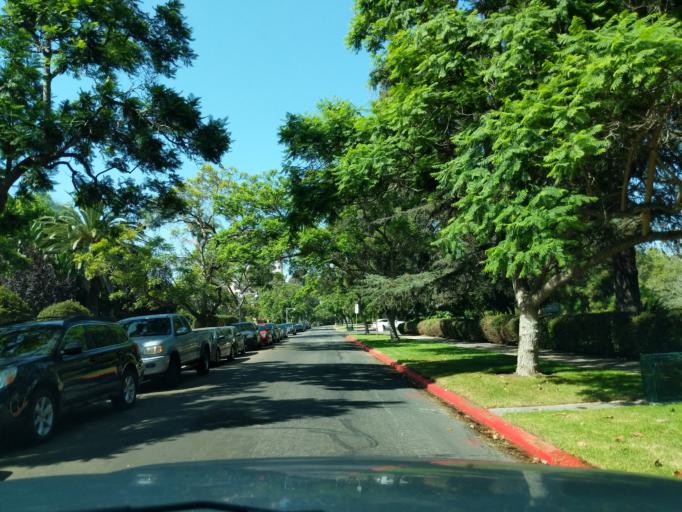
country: US
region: California
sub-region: San Diego County
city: San Diego
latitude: 32.7416
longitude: -117.1584
